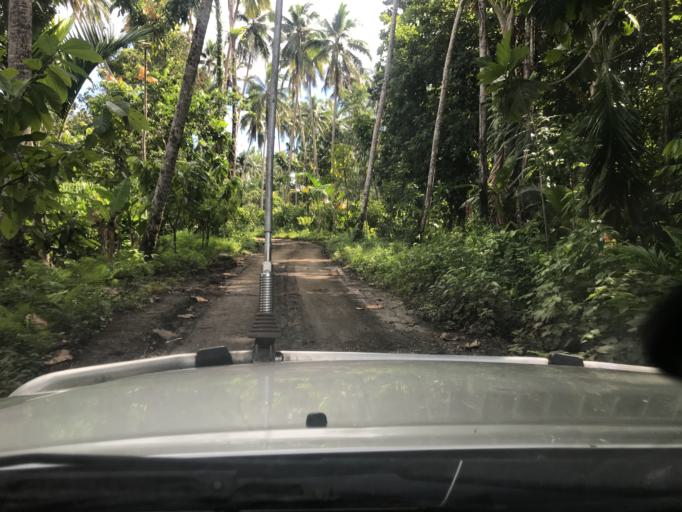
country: SB
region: Malaita
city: Auki
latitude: -8.9323
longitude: 160.7685
